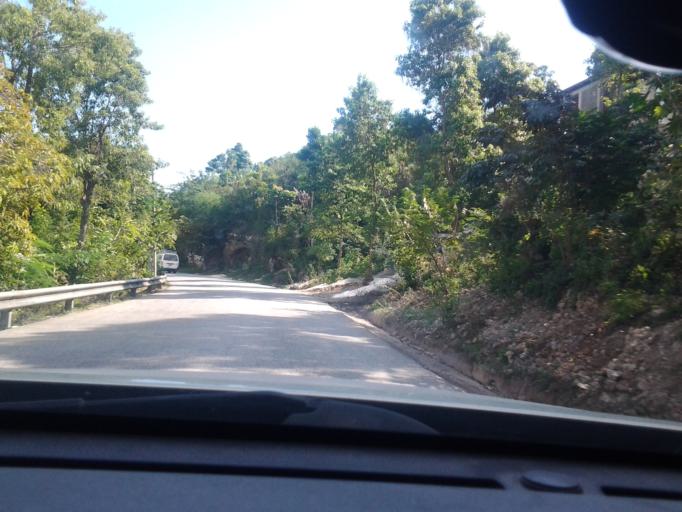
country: HT
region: Sud-Est
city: Jacmel
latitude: 18.2901
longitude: -72.5760
